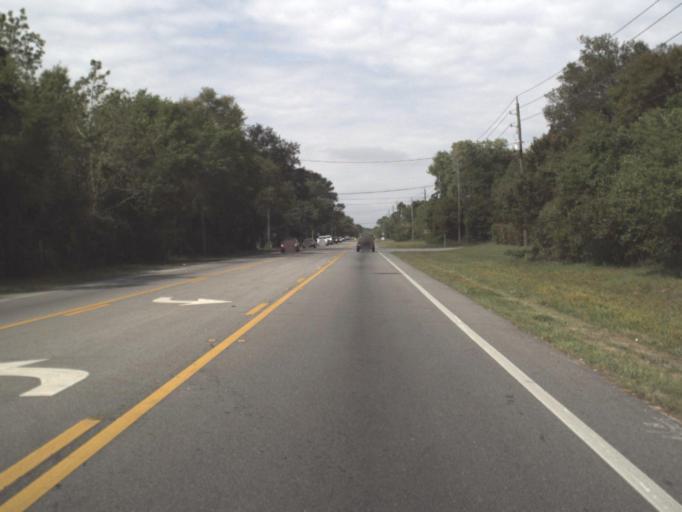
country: US
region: Florida
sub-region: Escambia County
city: Warrington
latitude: 30.3845
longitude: -87.2974
